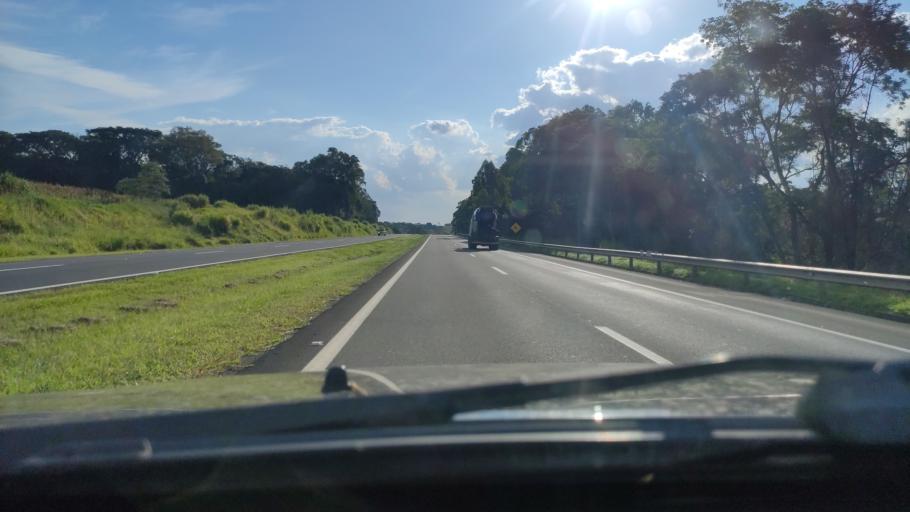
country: BR
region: Sao Paulo
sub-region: Itapira
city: Itapira
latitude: -22.4531
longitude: -46.8661
